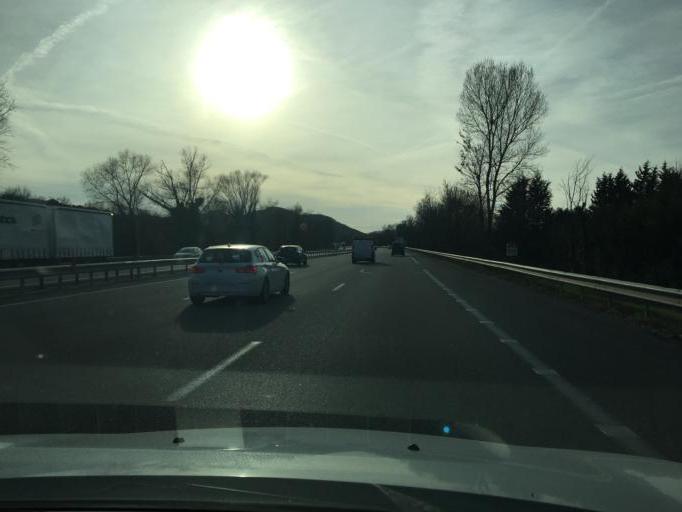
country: FR
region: Provence-Alpes-Cote d'Azur
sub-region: Departement du Var
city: Les Arcs
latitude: 43.4414
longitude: 6.4789
